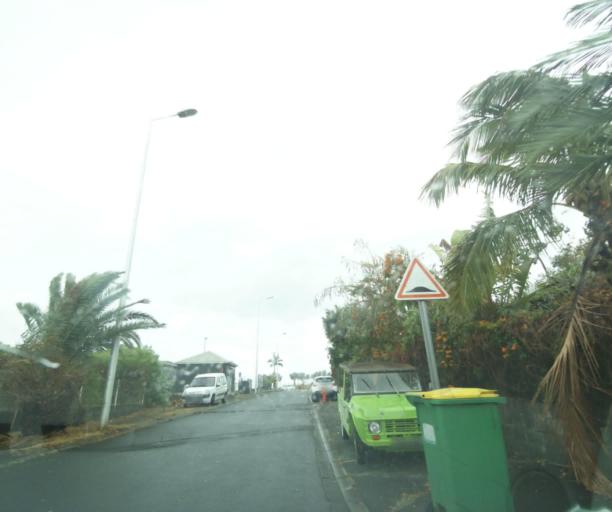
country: RE
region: Reunion
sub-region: Reunion
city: Saint-Paul
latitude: -21.0439
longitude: 55.2520
